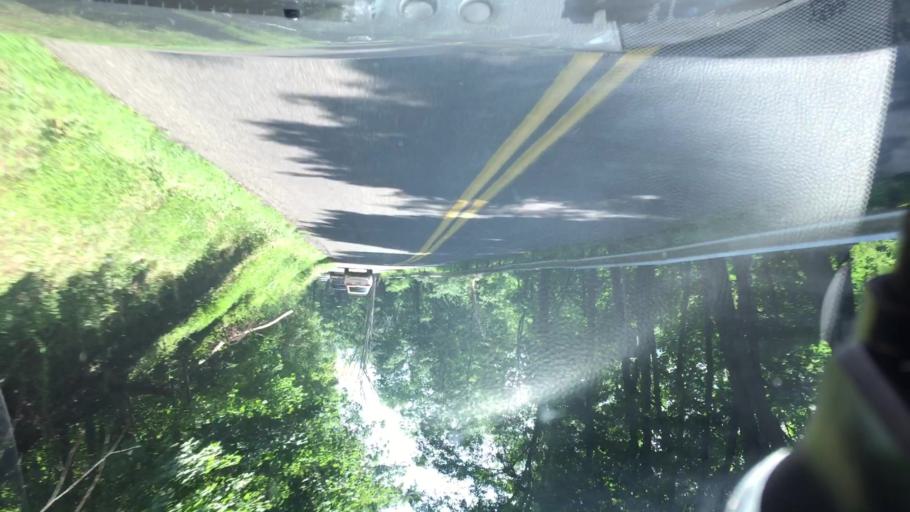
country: US
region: Pennsylvania
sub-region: Columbia County
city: Catawissa
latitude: 40.9549
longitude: -76.4474
